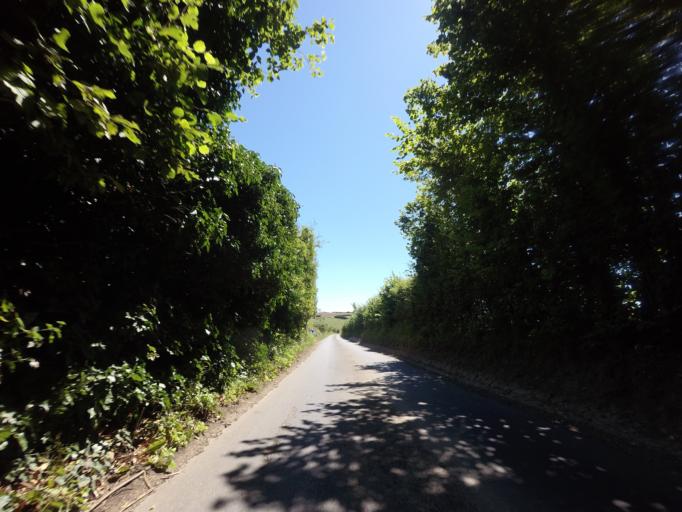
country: GB
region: England
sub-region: Kent
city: Eastry
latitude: 51.2050
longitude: 1.3046
